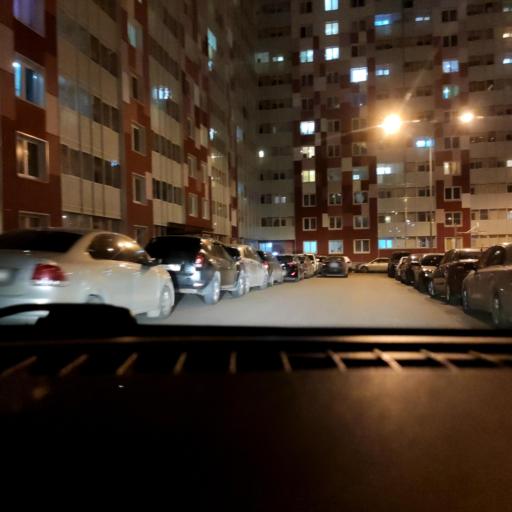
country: RU
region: Perm
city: Perm
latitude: 57.9907
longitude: 56.2674
